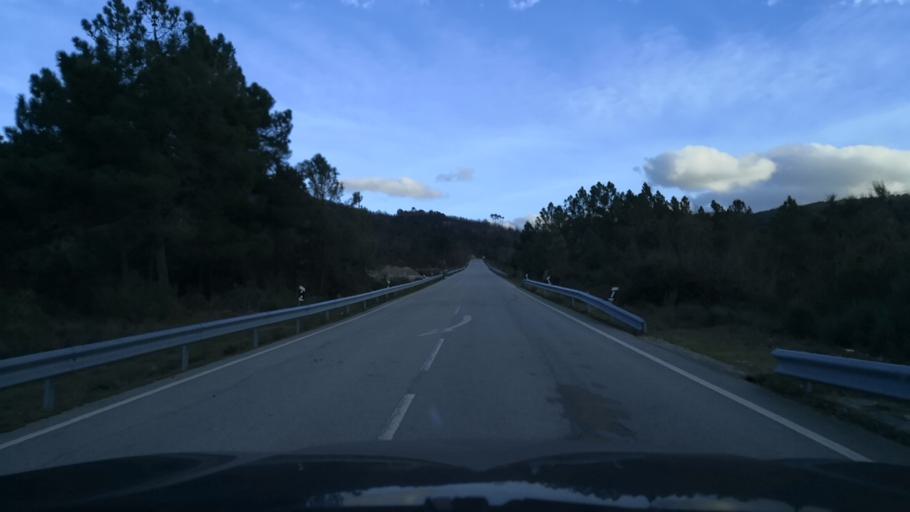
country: PT
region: Braganca
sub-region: Carrazeda de Ansiaes
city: Carrazeda de Anciaes
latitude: 41.2594
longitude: -7.3210
